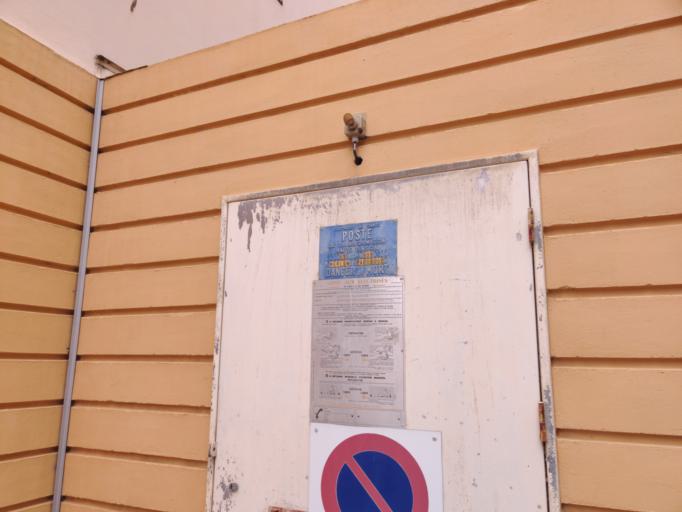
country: FR
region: Pays de la Loire
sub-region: Departement de la Vendee
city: Les Sables-d'Olonne
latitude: 46.5034
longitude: -1.7934
